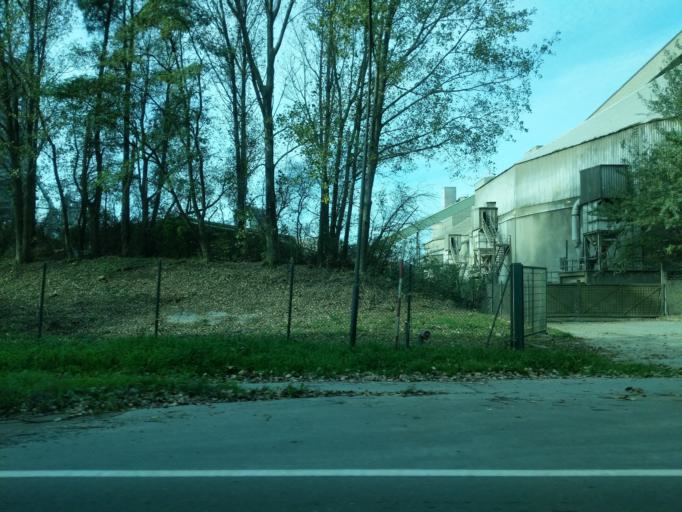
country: DE
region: Schleswig-Holstein
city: Lagerdorf
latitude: 53.8763
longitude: 9.5884
